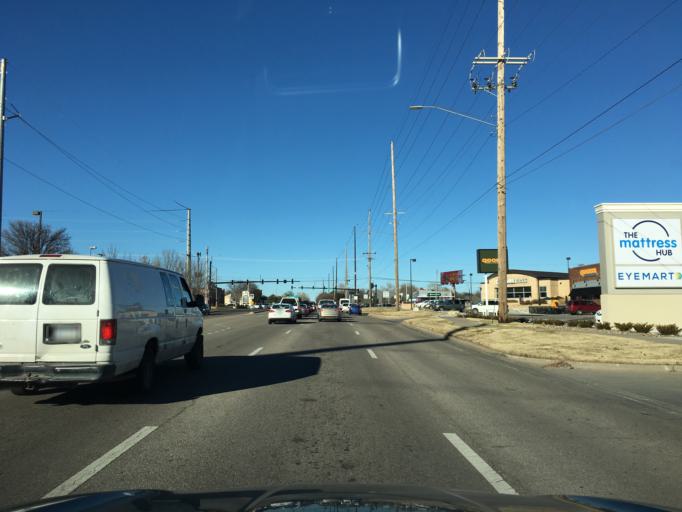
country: US
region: Kansas
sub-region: Sedgwick County
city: Bellaire
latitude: 37.6923
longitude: -97.2445
